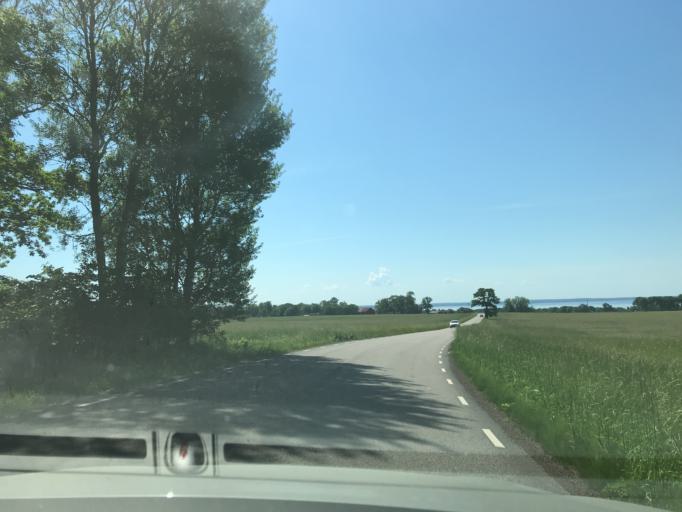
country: SE
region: Vaestra Goetaland
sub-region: Gotene Kommun
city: Kallby
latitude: 58.5518
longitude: 13.3438
